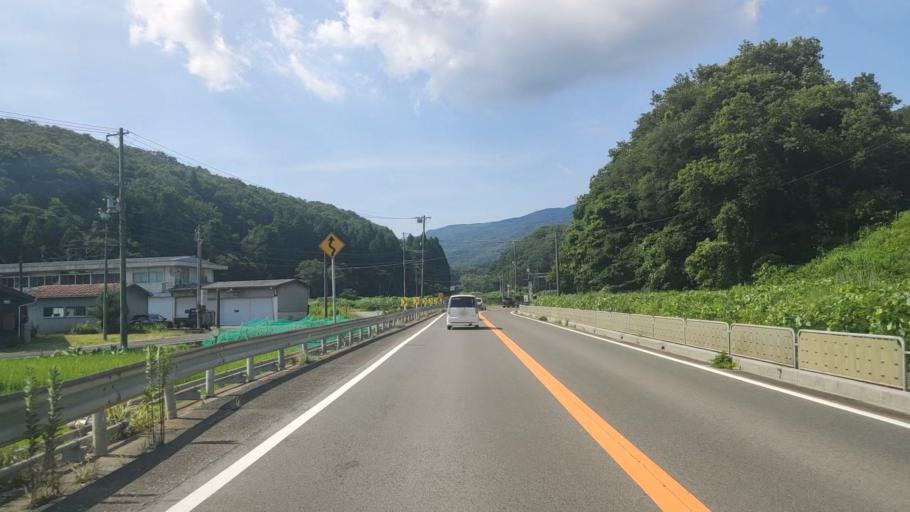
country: JP
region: Fukui
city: Tsuruga
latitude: 35.5422
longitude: 136.1496
